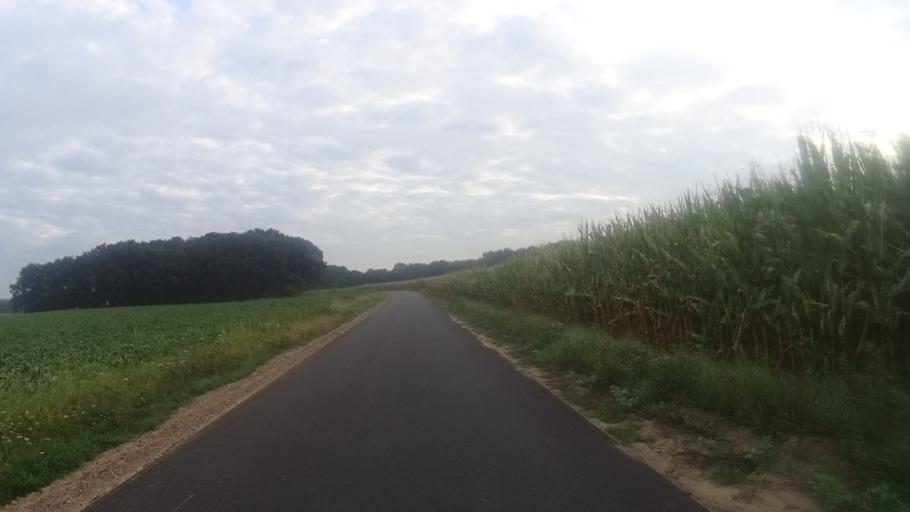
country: NL
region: Limburg
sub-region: Gemeente Venlo
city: Arcen
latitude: 51.4538
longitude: 6.1729
